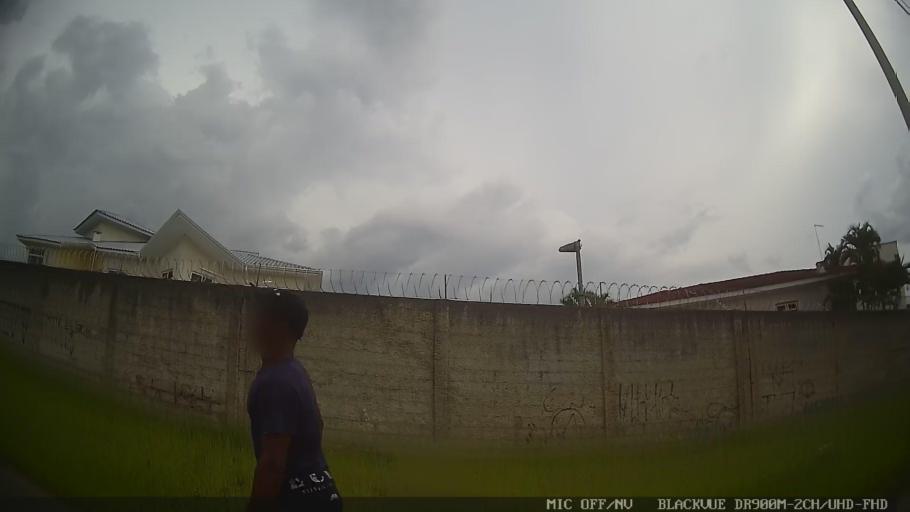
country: BR
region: Sao Paulo
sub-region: Suzano
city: Suzano
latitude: -23.5513
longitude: -46.2986
